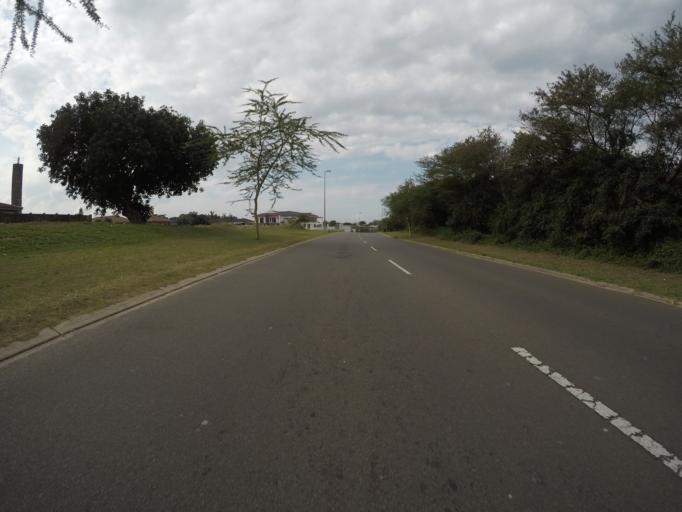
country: ZA
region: KwaZulu-Natal
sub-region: uThungulu District Municipality
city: Richards Bay
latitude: -28.7364
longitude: 32.0851
